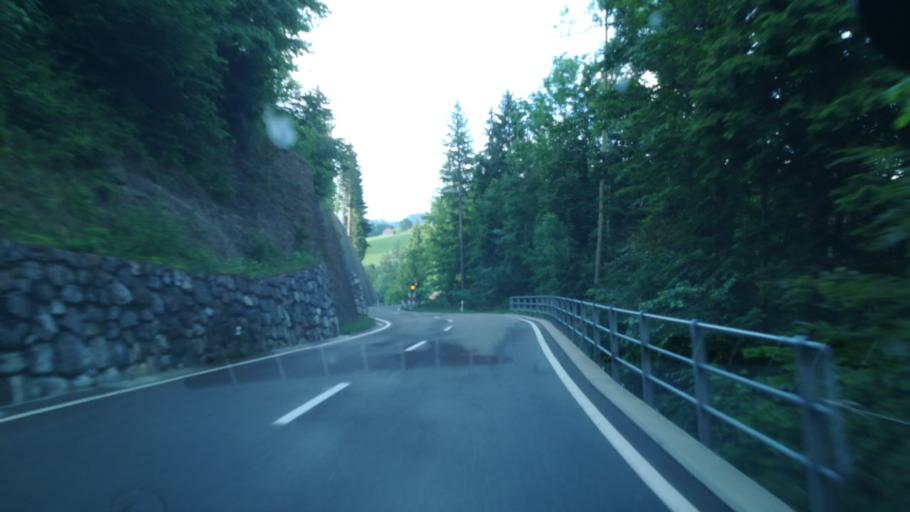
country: CH
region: Appenzell Ausserrhoden
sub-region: Bezirk Hinterland
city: Urnasch
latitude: 47.3240
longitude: 9.2965
